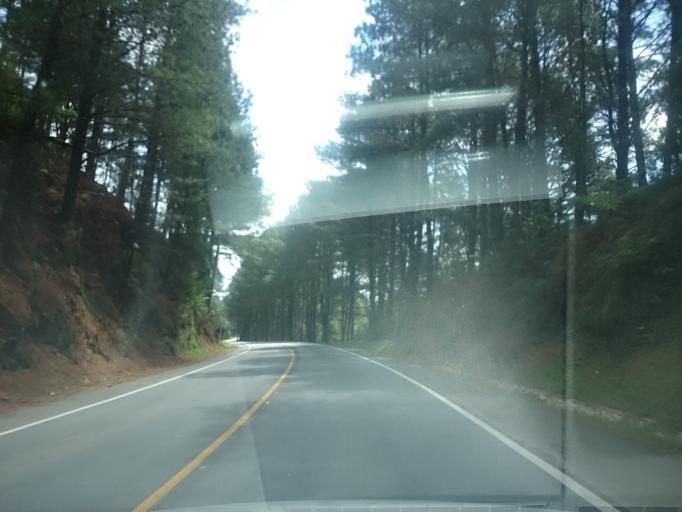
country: BR
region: Santa Catarina
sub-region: Santo Amaro Da Imperatriz
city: Santo Amaro da Imperatriz
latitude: -27.6791
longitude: -49.0075
